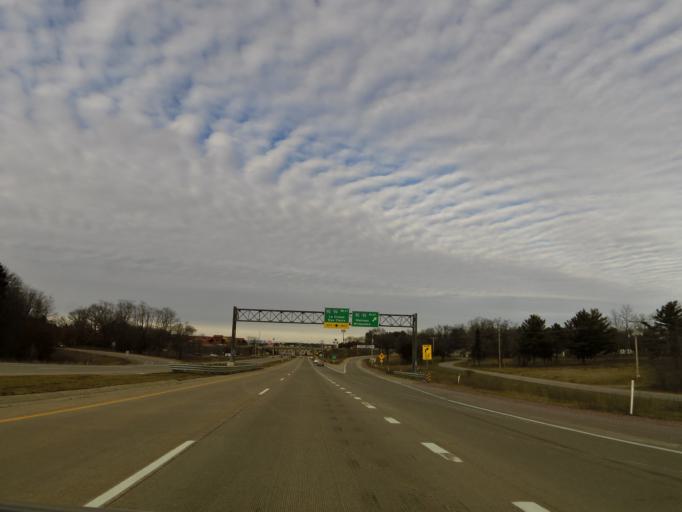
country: US
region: Wisconsin
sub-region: Sauk County
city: Lake Delton
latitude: 43.5658
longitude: -89.7784
